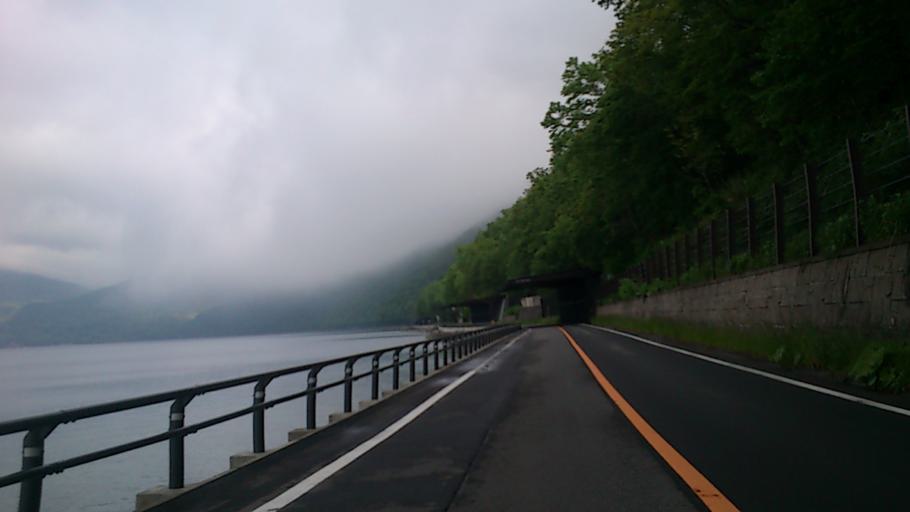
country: JP
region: Hokkaido
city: Shiraoi
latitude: 42.7920
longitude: 141.3703
